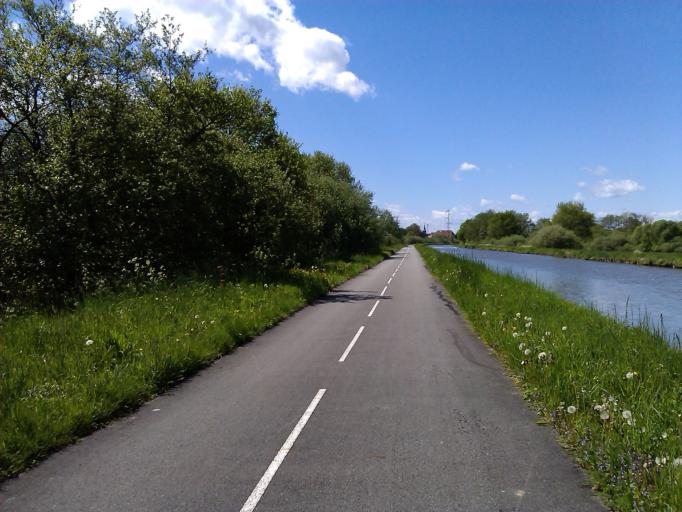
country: FR
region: Franche-Comte
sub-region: Territoire de Belfort
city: Morvillars
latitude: 47.5722
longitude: 6.9525
